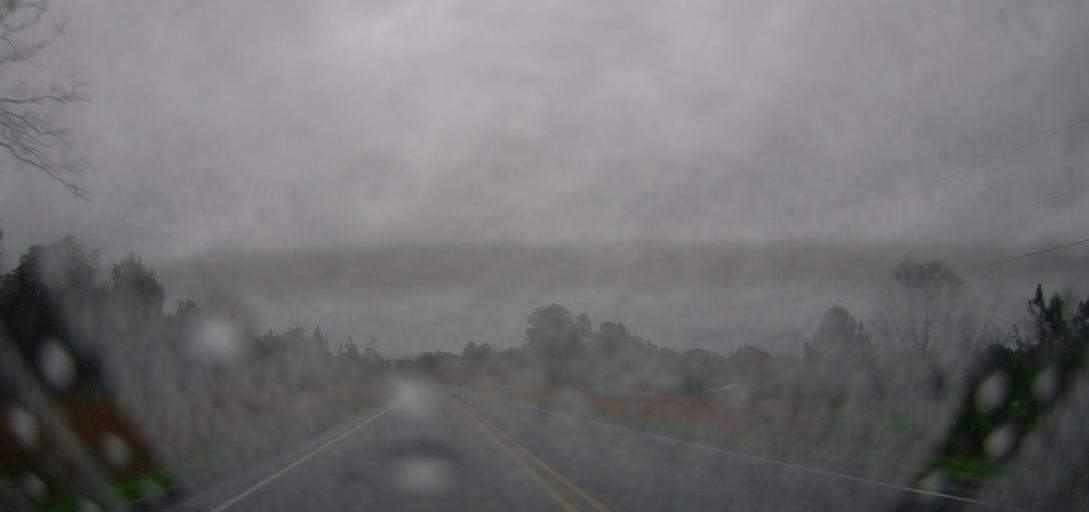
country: US
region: Alabama
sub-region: Chilton County
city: Clanton
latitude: 32.6345
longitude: -86.7485
